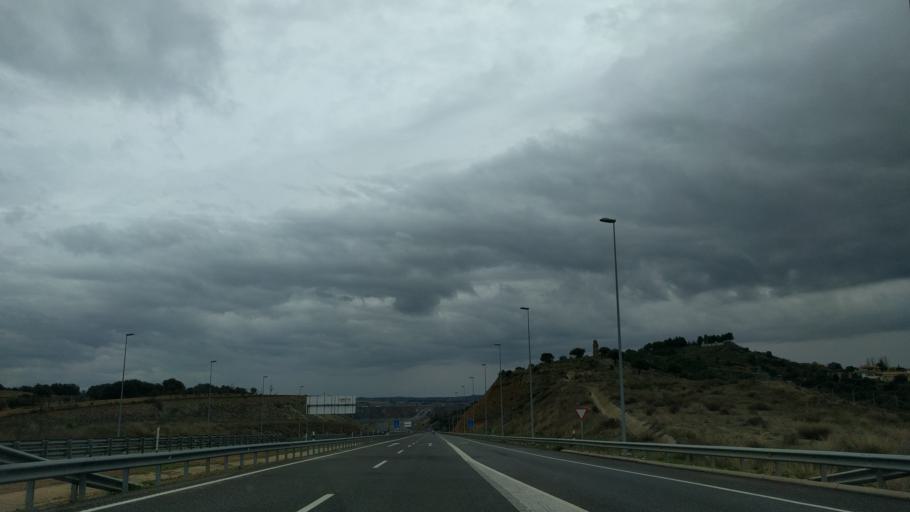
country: ES
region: Aragon
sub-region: Provincia de Huesca
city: Castejon del Puente
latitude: 41.9687
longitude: 0.1542
